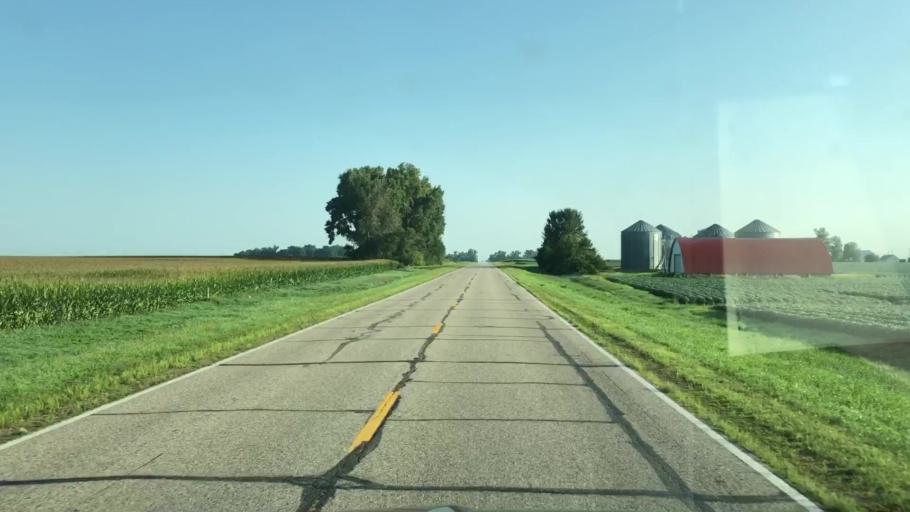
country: US
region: Iowa
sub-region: Lyon County
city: George
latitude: 43.3991
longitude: -95.9982
